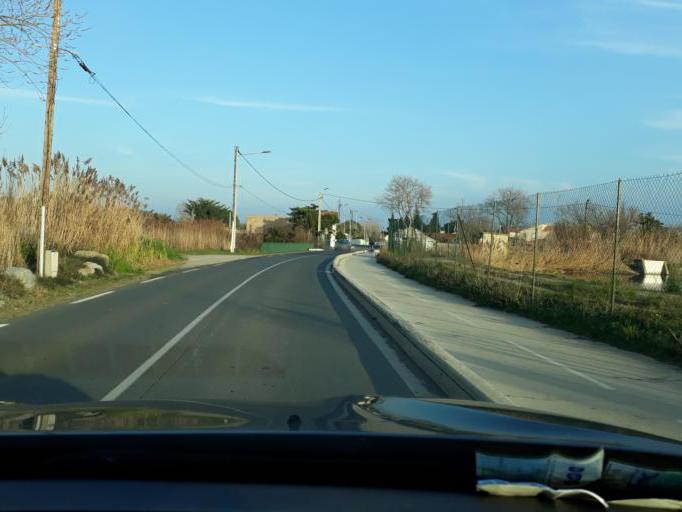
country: FR
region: Languedoc-Roussillon
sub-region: Departement de l'Herault
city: Marseillan
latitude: 43.3211
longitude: 3.5334
